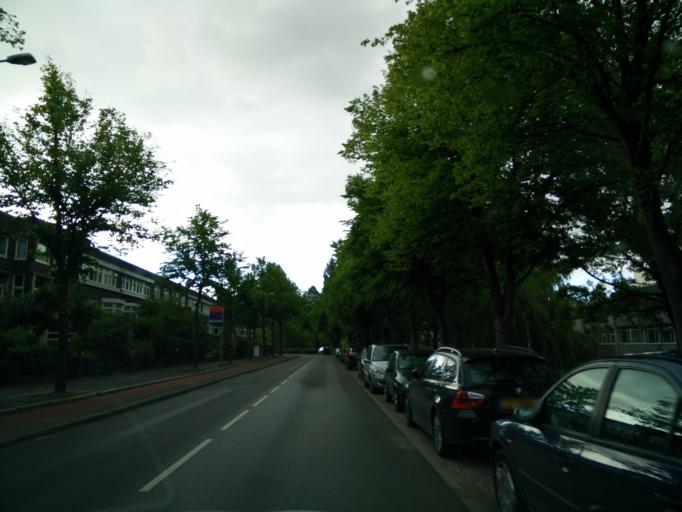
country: NL
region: Groningen
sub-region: Gemeente Groningen
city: Korrewegwijk
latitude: 53.2259
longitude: 6.5727
